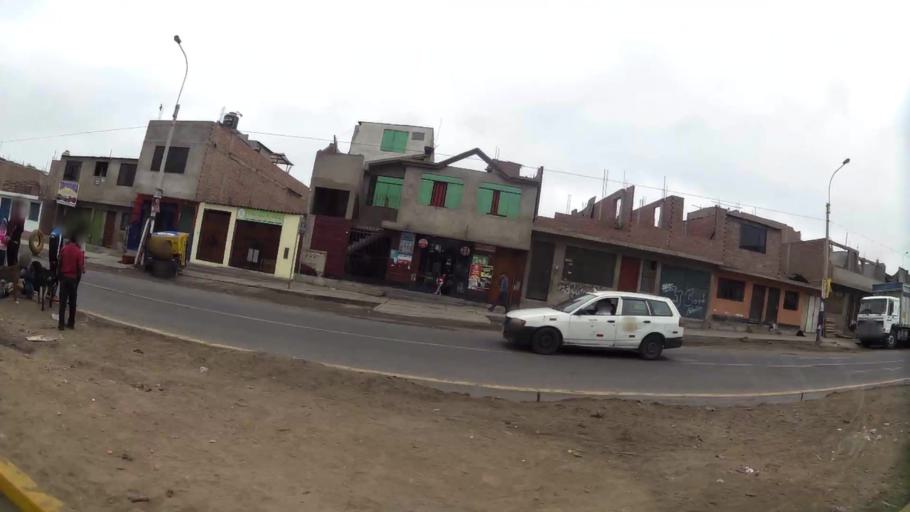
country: PE
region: Lima
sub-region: Lima
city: Surco
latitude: -12.1924
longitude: -76.9828
